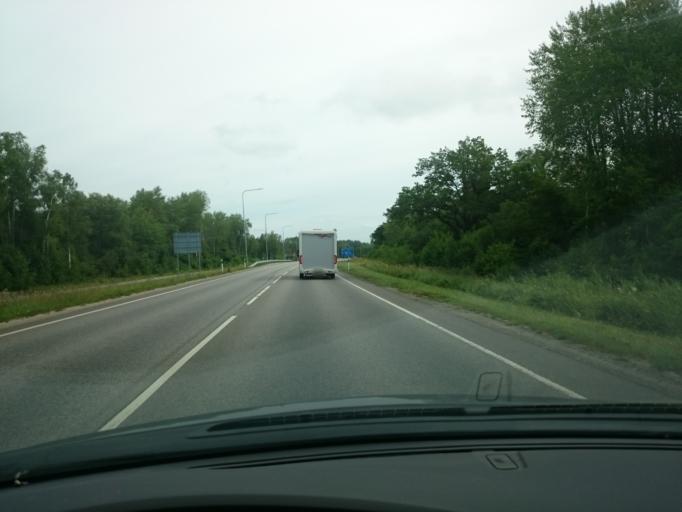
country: EE
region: Laeaene
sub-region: Ridala Parish
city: Uuemoisa
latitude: 58.9550
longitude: 23.6628
